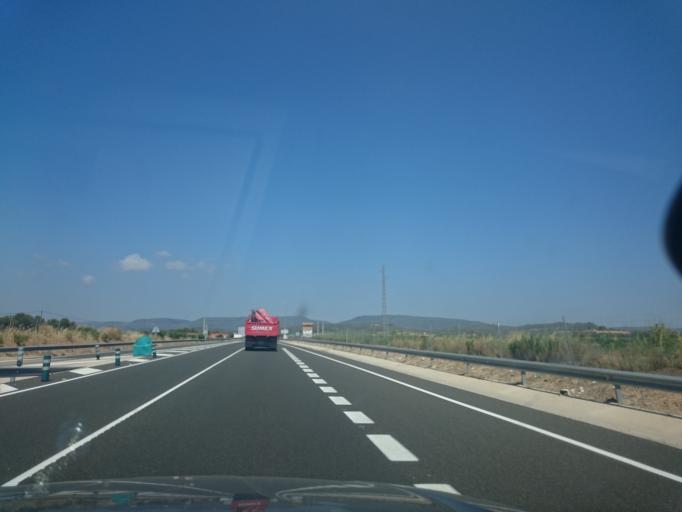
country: ES
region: Catalonia
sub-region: Provincia de Barcelona
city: el Pla del Penedes
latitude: 41.4189
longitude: 1.6918
